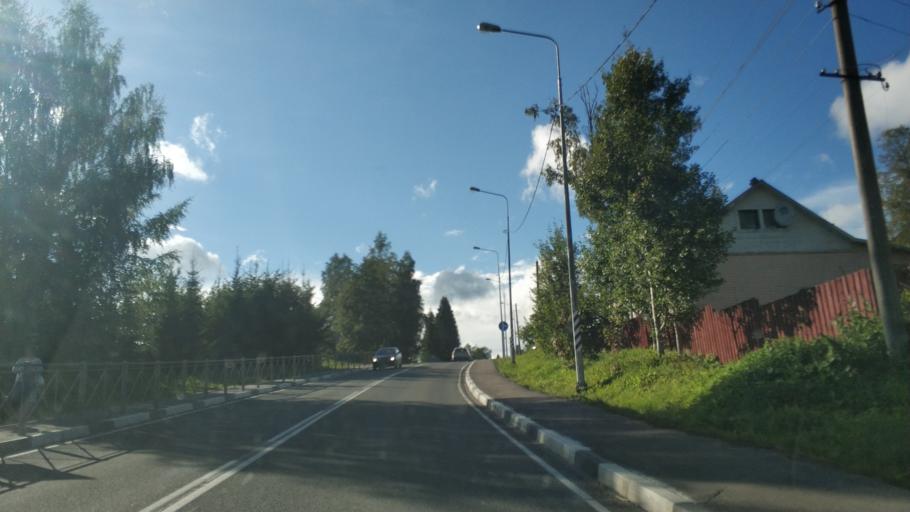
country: RU
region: Republic of Karelia
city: Lakhdenpokh'ya
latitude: 61.5222
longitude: 30.1866
